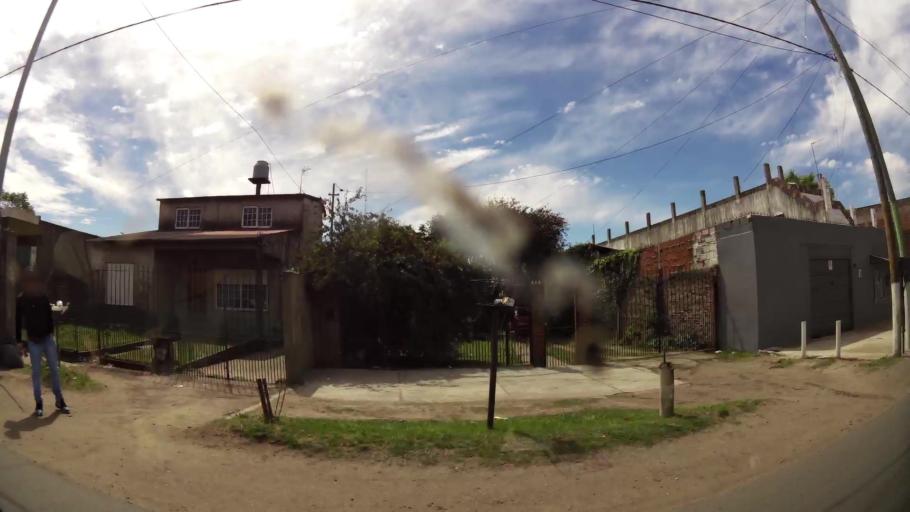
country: AR
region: Buenos Aires
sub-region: Partido de Quilmes
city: Quilmes
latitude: -34.7767
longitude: -58.2860
